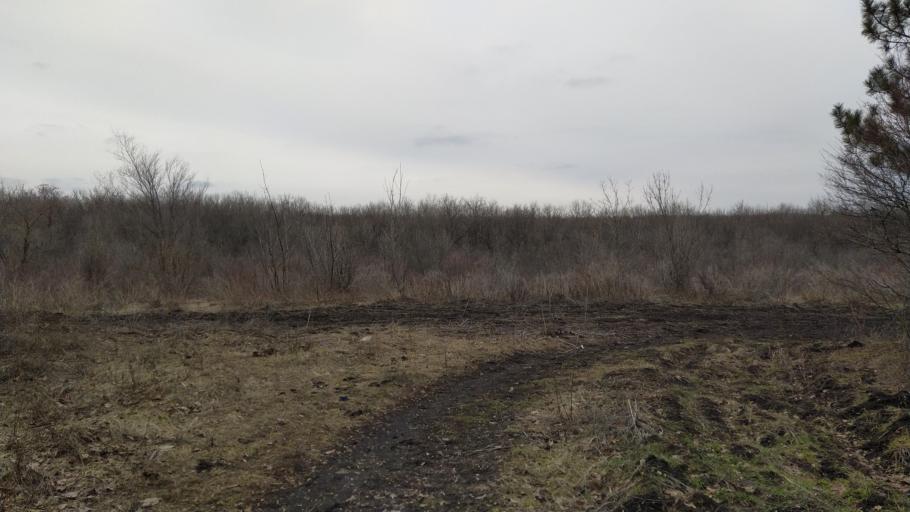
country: RU
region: Rostov
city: Temernik
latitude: 47.3498
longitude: 39.7472
